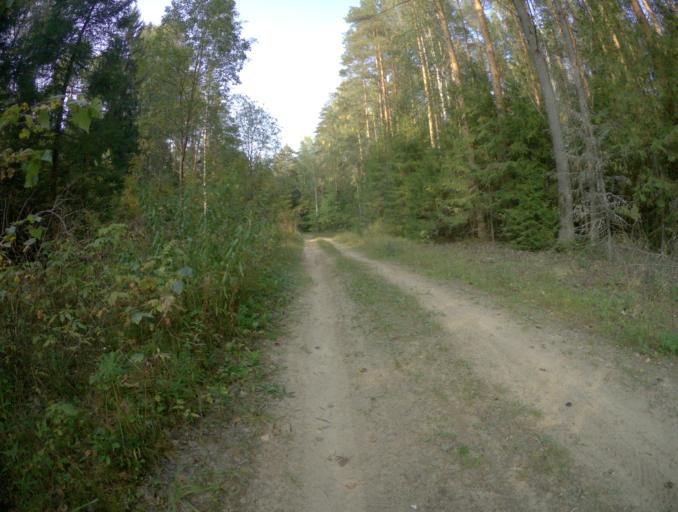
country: RU
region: Vladimir
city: Golovino
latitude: 55.9970
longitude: 40.4514
